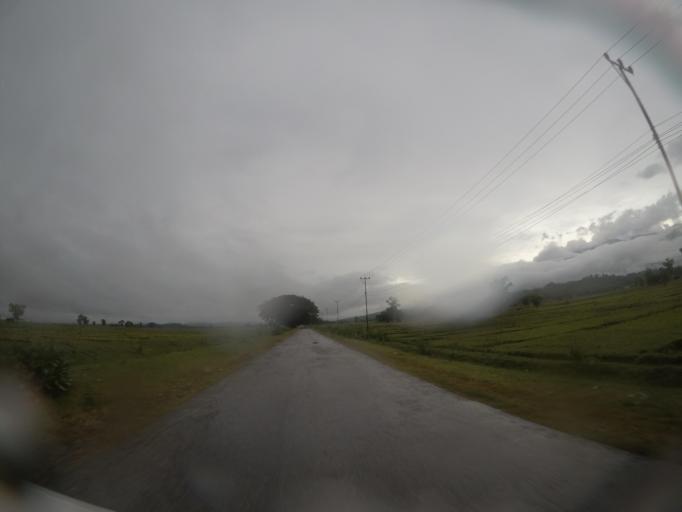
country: TL
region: Bobonaro
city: Maliana
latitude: -8.9914
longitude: 125.1760
